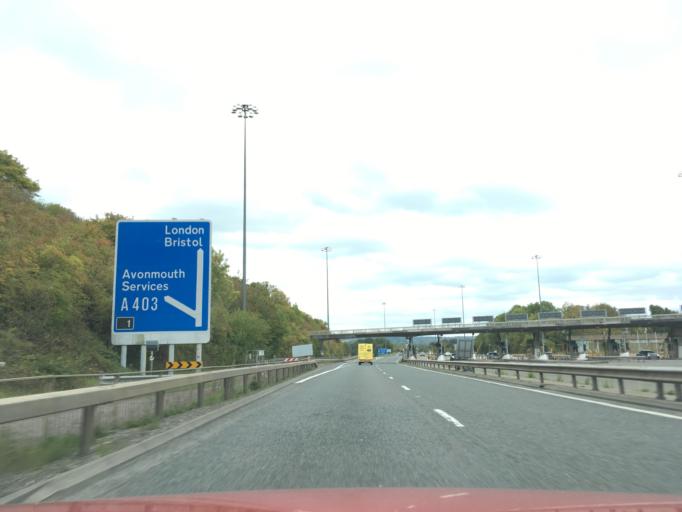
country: GB
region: England
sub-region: South Gloucestershire
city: Severn Beach
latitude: 51.6041
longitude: -2.6246
